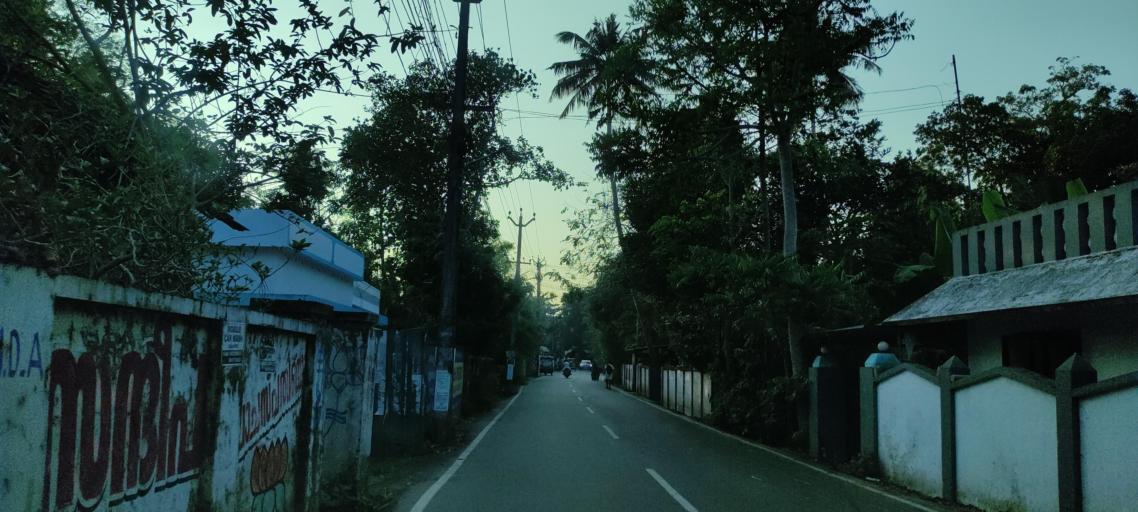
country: IN
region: Kerala
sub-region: Alappuzha
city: Alleppey
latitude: 9.5401
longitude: 76.3360
